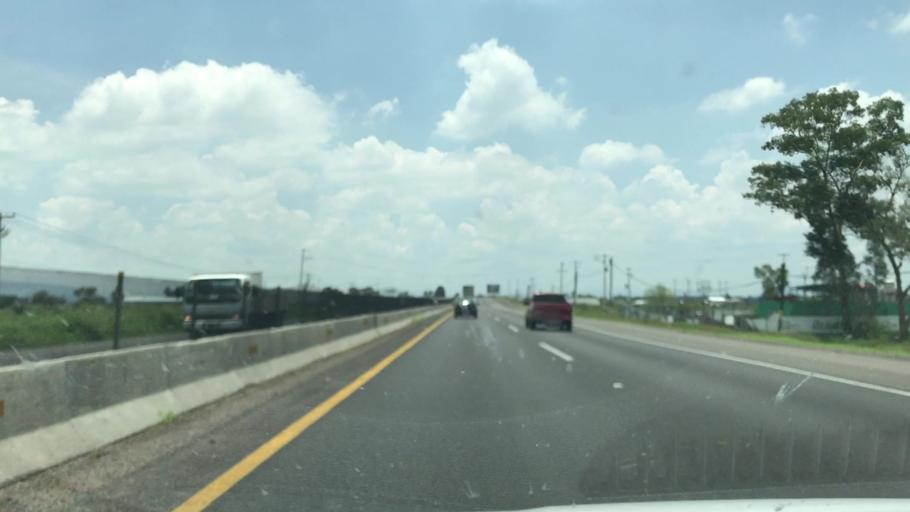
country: MX
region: Guanajuato
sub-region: Irapuato
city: San Jose de Bernalejo (El Guayabo)
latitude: 20.6101
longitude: -101.4089
